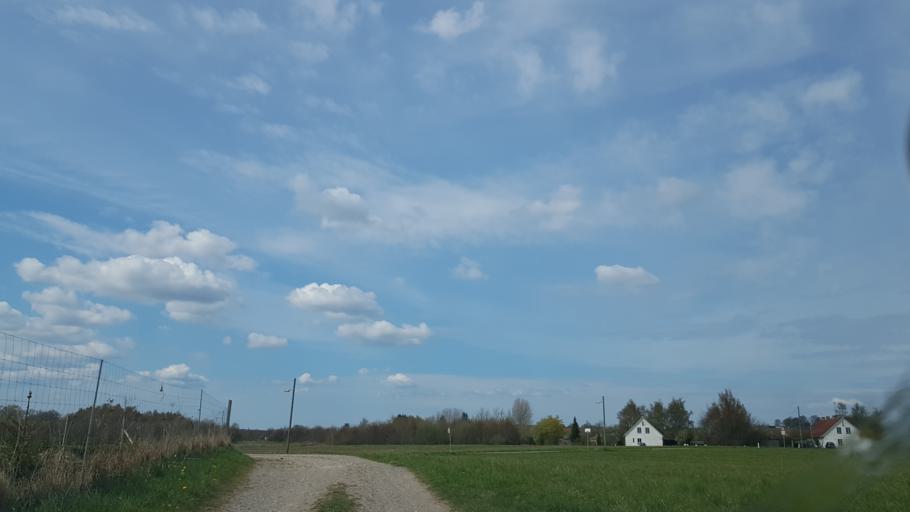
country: DK
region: Capital Region
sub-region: Allerod Kommune
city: Lillerod
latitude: 55.8982
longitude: 12.3350
